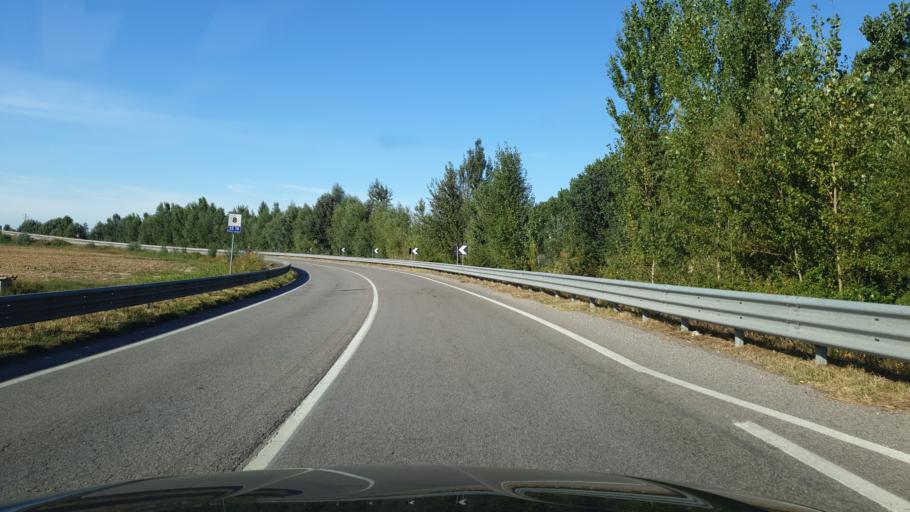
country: IT
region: Emilia-Romagna
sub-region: Provincia di Ravenna
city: Alfonsine
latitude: 44.5013
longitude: 12.0614
